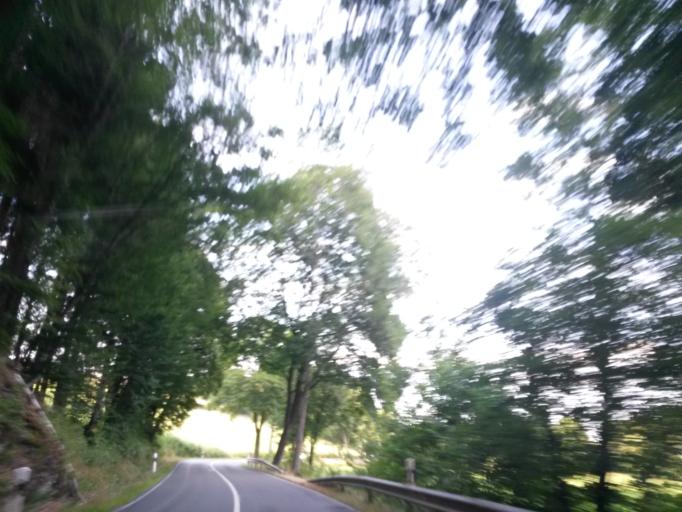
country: DE
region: North Rhine-Westphalia
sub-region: Regierungsbezirk Koln
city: Marienheide
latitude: 51.0517
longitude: 7.4951
